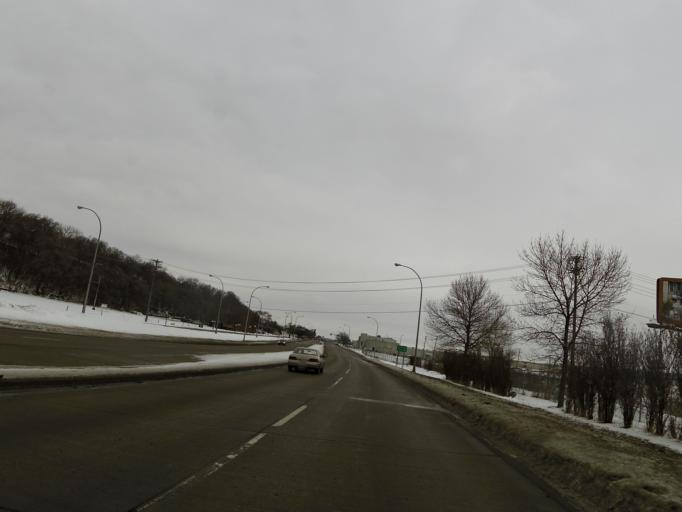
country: US
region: Minnesota
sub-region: Dakota County
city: South Saint Paul
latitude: 44.8826
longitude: -93.0317
